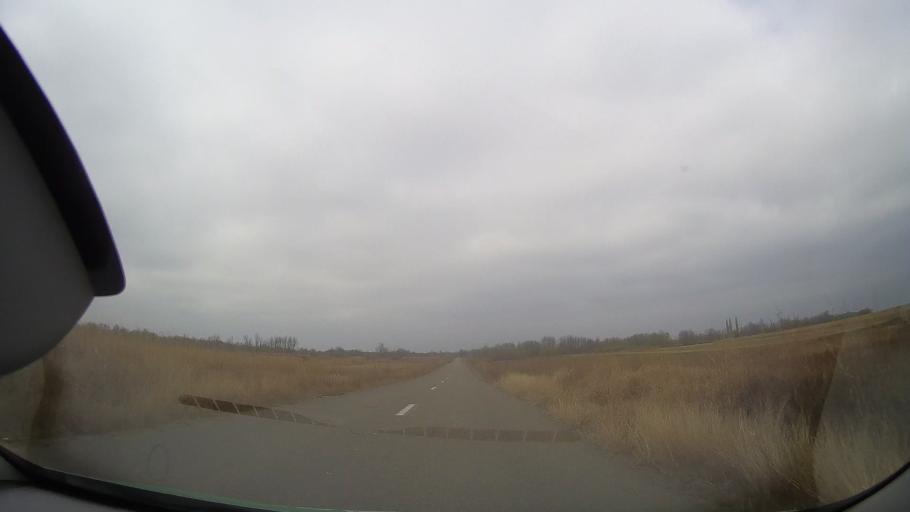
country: RO
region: Buzau
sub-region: Comuna Scutelnici
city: Scutelnici
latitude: 44.8709
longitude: 26.8881
